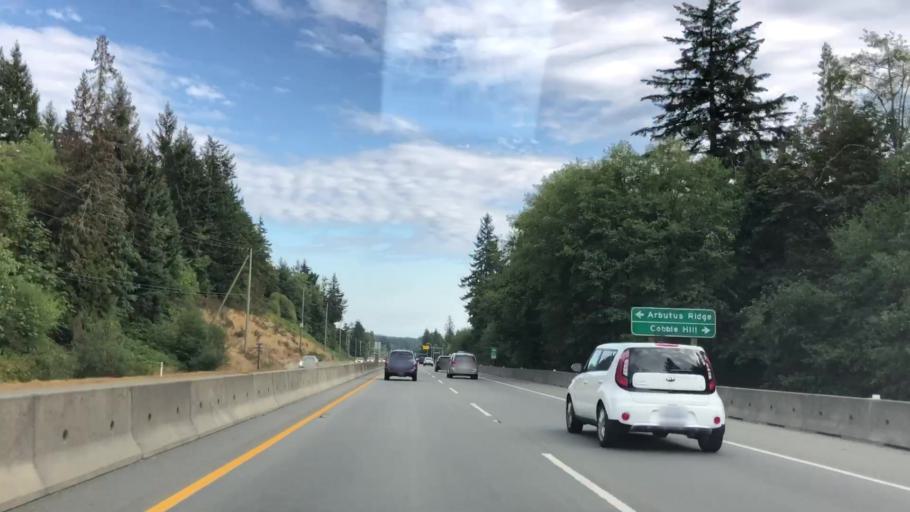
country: CA
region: British Columbia
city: Duncan
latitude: 48.6898
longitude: -123.5833
